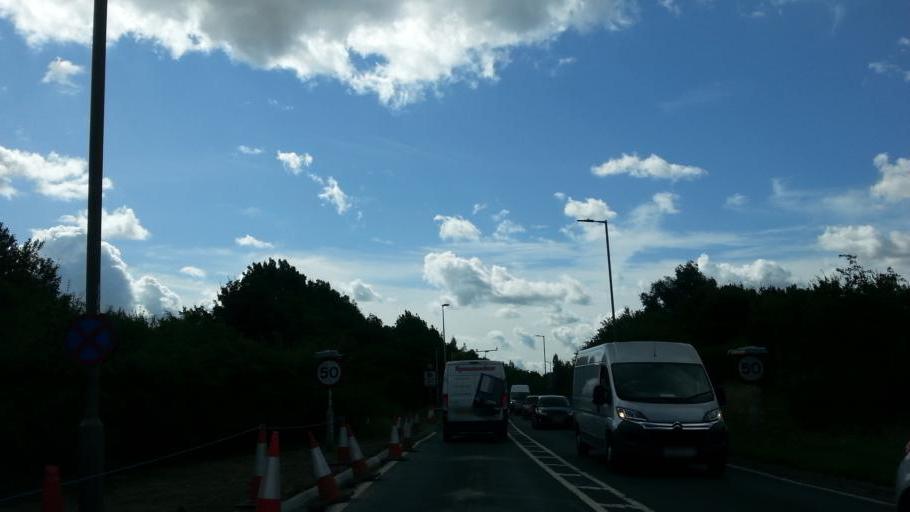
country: GB
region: England
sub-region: Essex
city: South Benfleet
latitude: 51.5649
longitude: 0.5422
